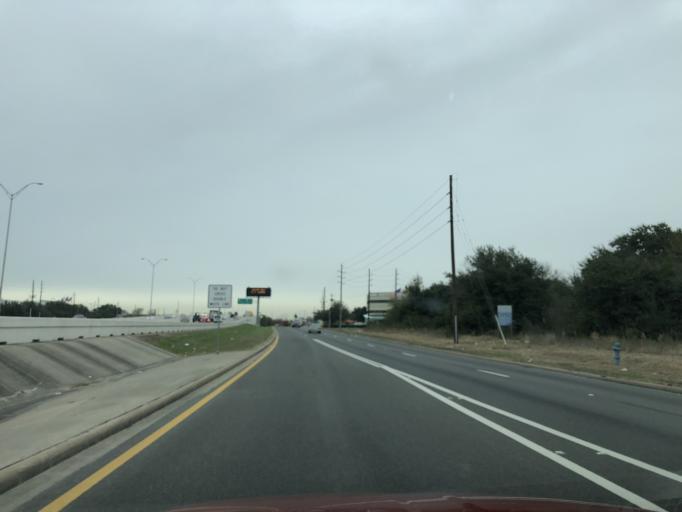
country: US
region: Texas
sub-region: Fort Bend County
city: Missouri City
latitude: 29.6414
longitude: -95.5354
